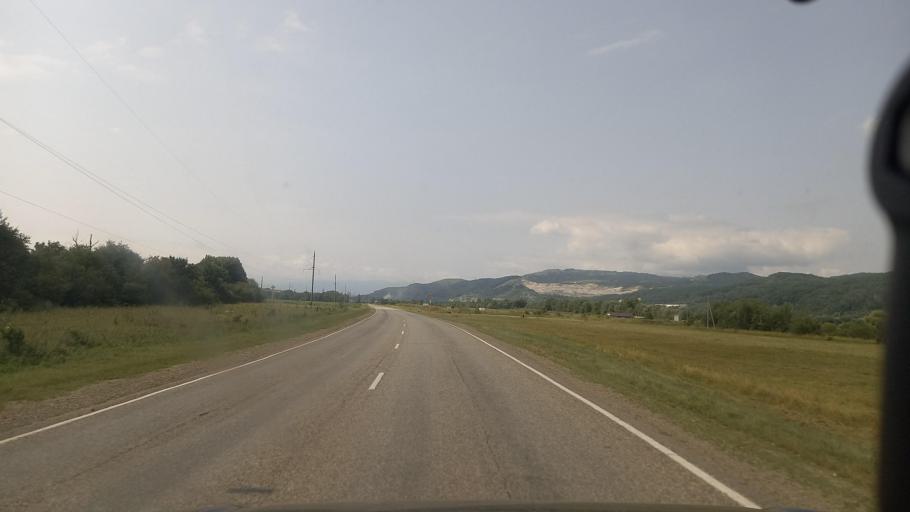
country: RU
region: Krasnodarskiy
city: Shedok
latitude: 44.2026
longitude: 40.8485
